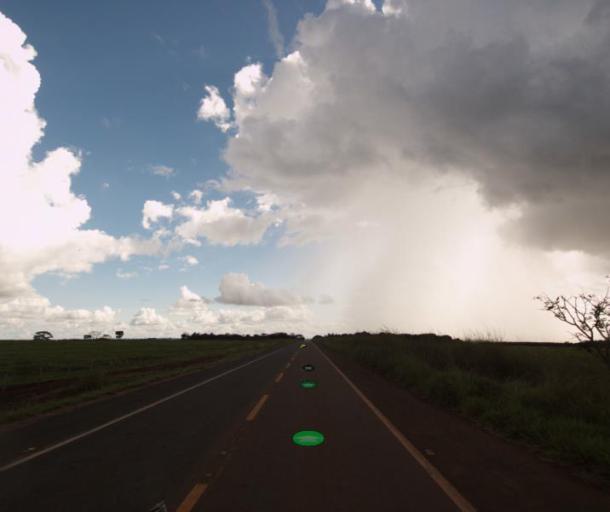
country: BR
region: Goias
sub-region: Itaberai
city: Itaberai
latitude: -15.9933
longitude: -49.7321
